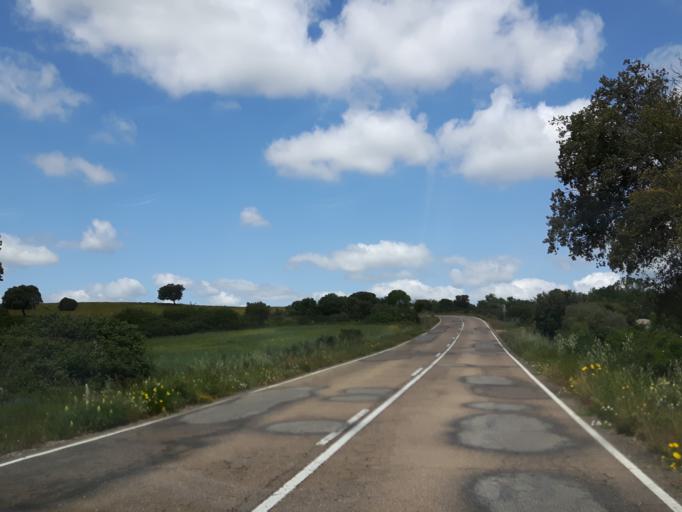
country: ES
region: Castille and Leon
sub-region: Provincia de Salamanca
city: Villar de la Yegua
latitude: 40.7144
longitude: -6.6865
